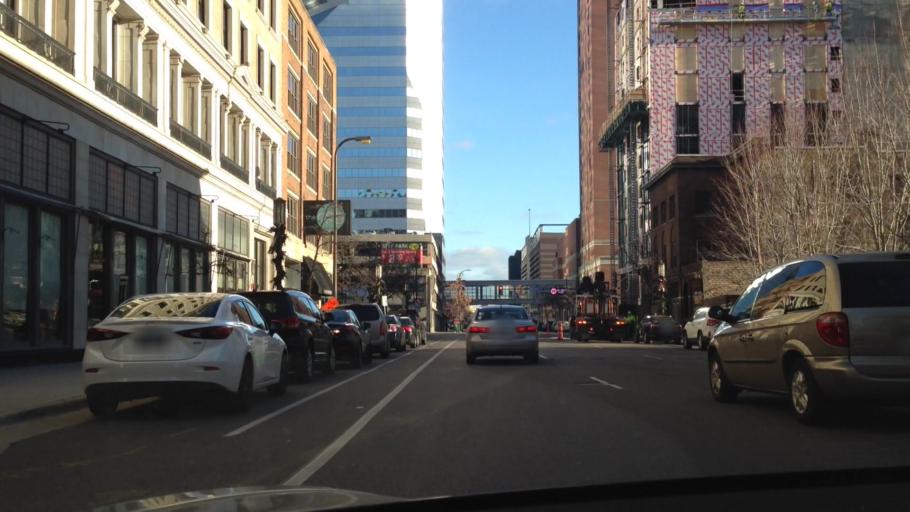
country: US
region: Minnesota
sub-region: Hennepin County
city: Minneapolis
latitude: 44.9739
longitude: -93.2747
